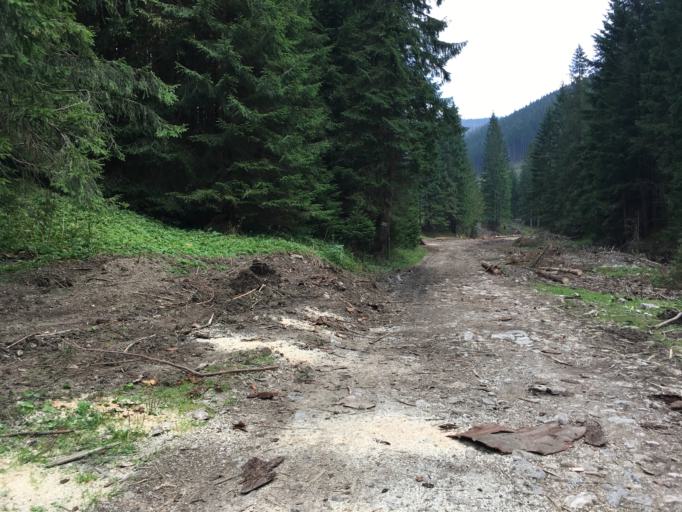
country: PL
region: Lesser Poland Voivodeship
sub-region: Powiat tatrzanski
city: Koscielisko
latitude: 49.2657
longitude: 19.8437
